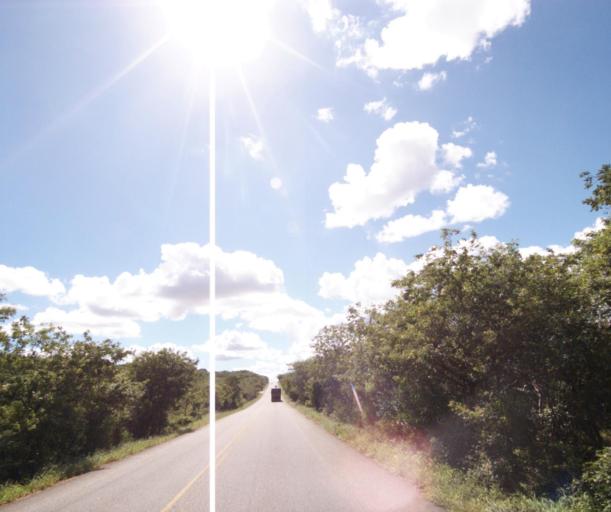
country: BR
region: Bahia
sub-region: Caetite
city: Caetite
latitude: -14.1718
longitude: -42.2055
